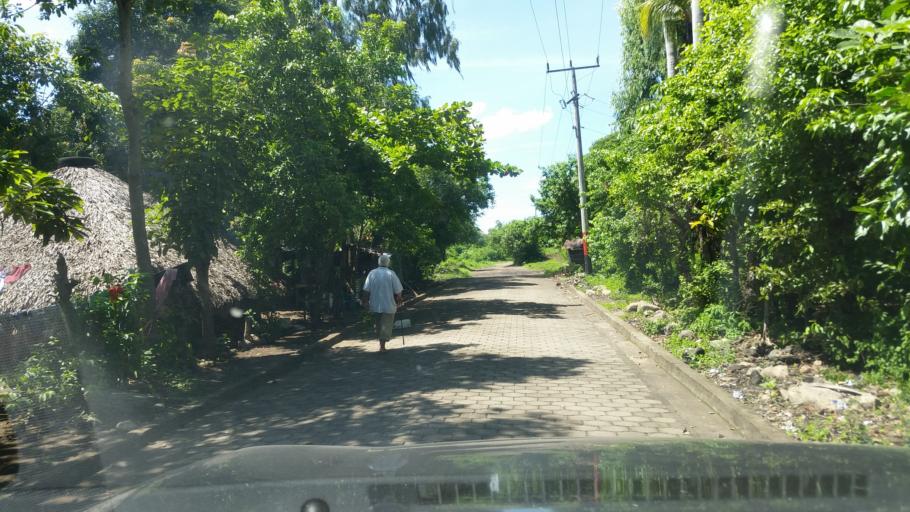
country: NI
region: Chinandega
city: Puerto Morazan
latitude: 12.7653
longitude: -87.1345
